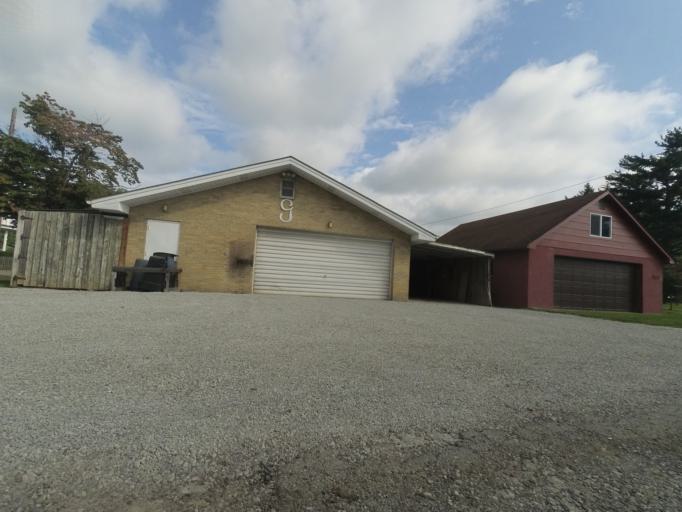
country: US
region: West Virginia
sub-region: Cabell County
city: Huntington
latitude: 38.4350
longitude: -82.4057
